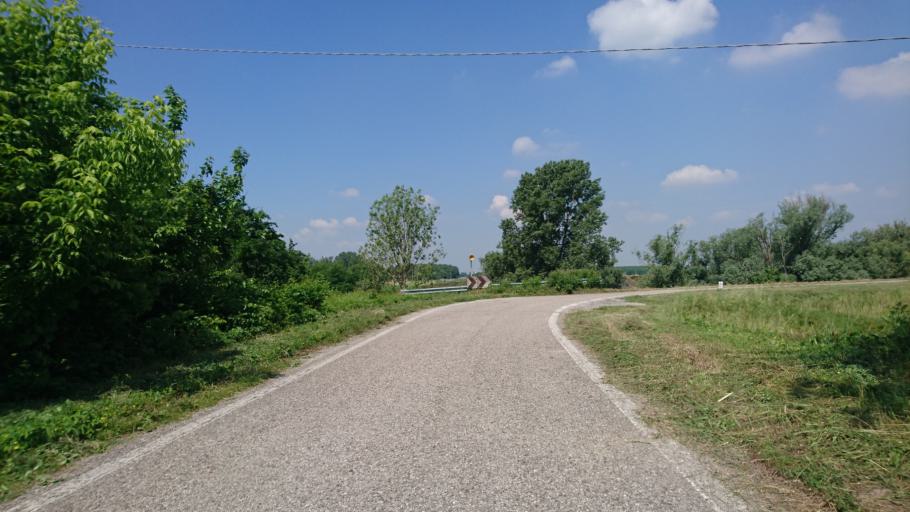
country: IT
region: Lombardy
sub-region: Provincia di Mantova
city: Sustinente
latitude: 45.0756
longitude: 10.9783
